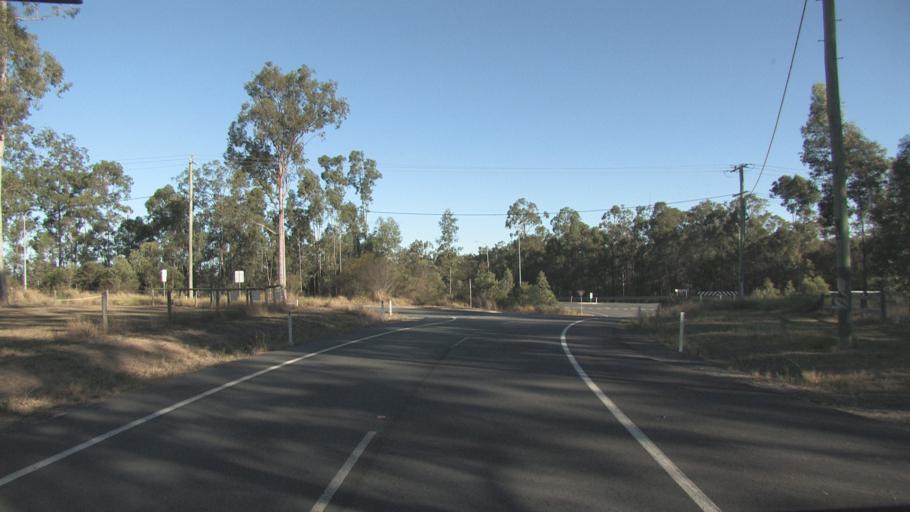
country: AU
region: Queensland
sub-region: Logan
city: North Maclean
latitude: -27.7569
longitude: 153.0204
